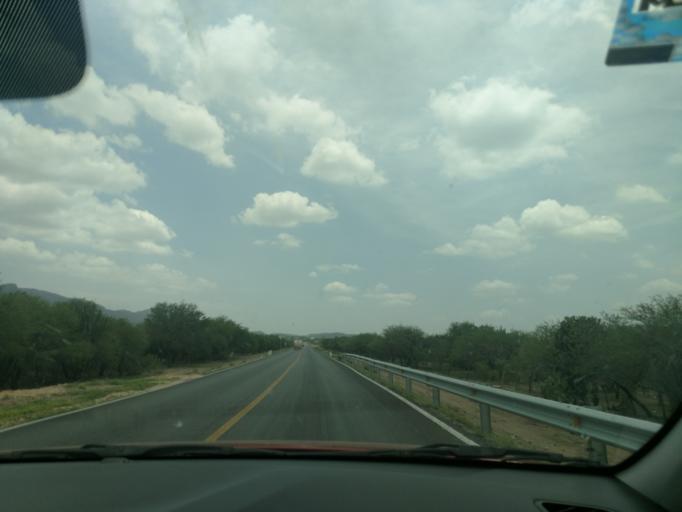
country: MX
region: San Luis Potosi
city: Zaragoza
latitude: 22.0185
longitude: -100.3975
